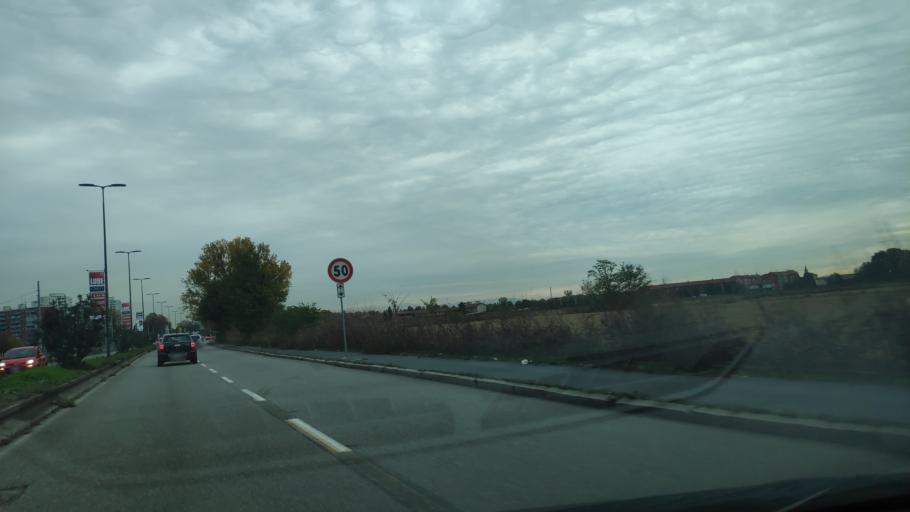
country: IT
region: Lombardy
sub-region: Citta metropolitana di Milano
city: Rozzano
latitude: 45.3985
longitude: 9.1738
